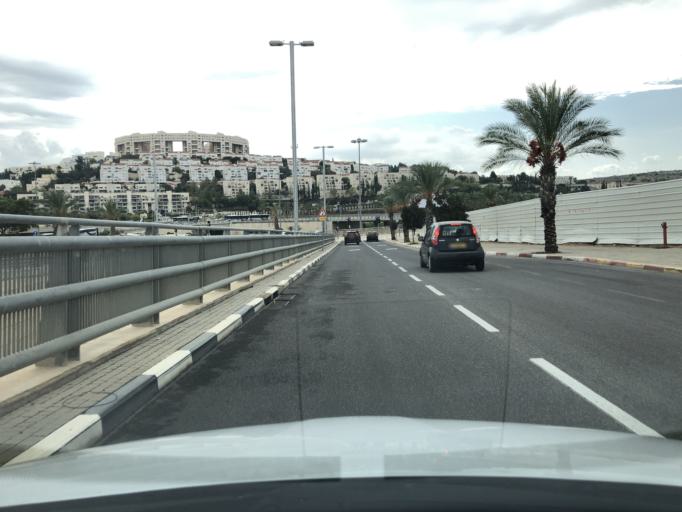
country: IL
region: Central District
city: Modiin
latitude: 31.9014
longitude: 35.0050
